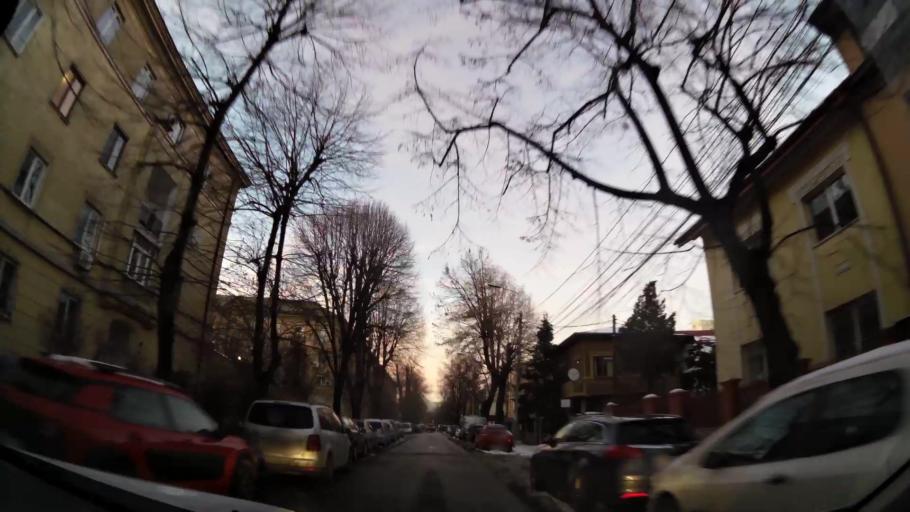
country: RO
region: Ilfov
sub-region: Comuna Fundeni-Dobroesti
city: Fundeni
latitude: 44.4371
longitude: 26.1418
